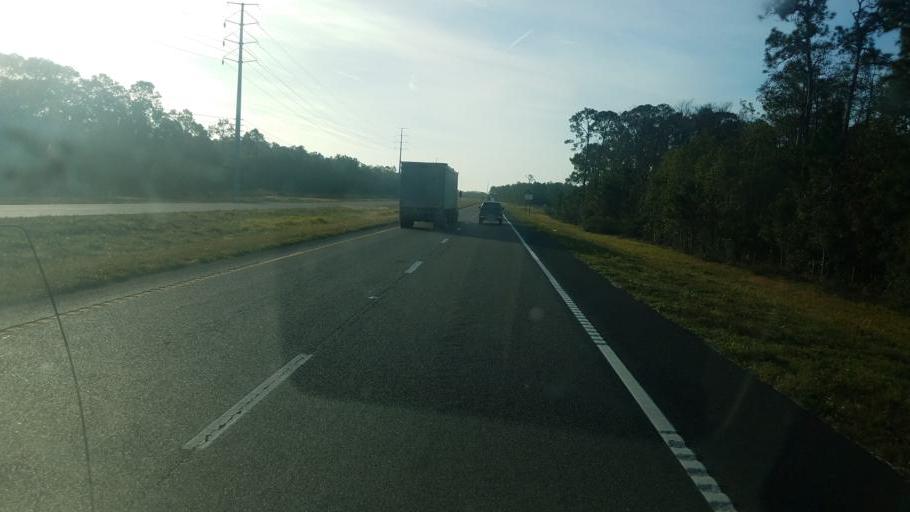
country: US
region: Florida
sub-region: Osceola County
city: Saint Cloud
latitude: 28.2044
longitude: -81.1698
